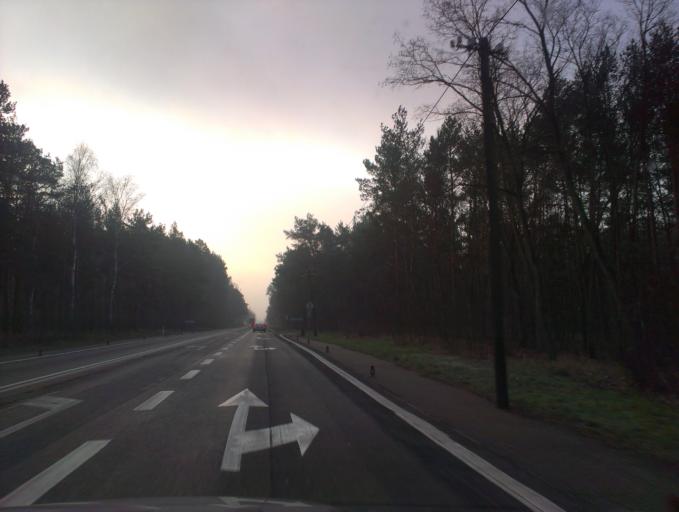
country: PL
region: Greater Poland Voivodeship
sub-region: Powiat chodzieski
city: Budzyn
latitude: 52.8378
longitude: 16.9728
